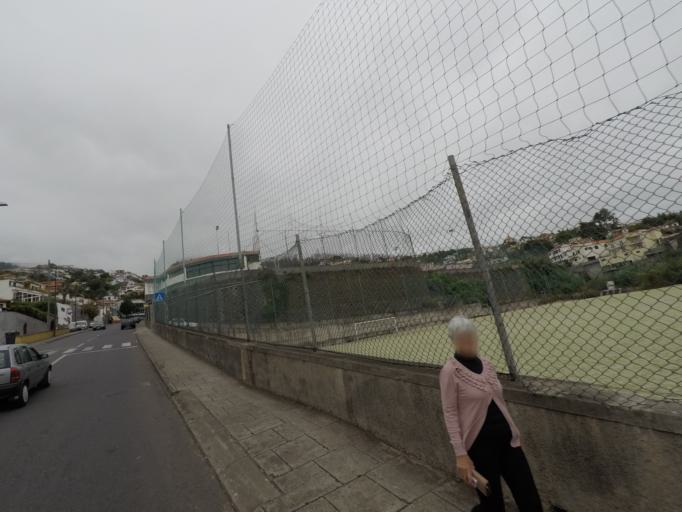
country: PT
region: Madeira
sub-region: Funchal
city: Nossa Senhora do Monte
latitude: 32.6696
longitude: -16.9368
